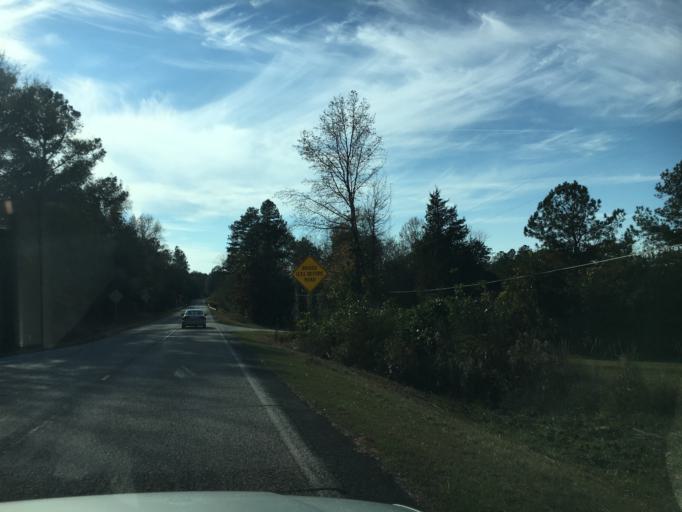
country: US
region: Georgia
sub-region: Hart County
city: Hartwell
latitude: 34.2714
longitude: -82.8729
